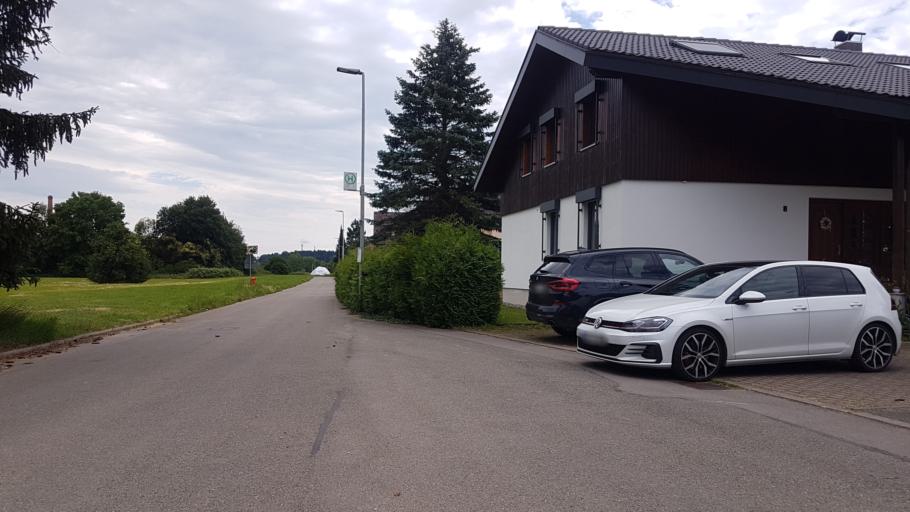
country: DE
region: Baden-Wuerttemberg
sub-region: Tuebingen Region
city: Scheer
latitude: 48.0718
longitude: 9.2959
